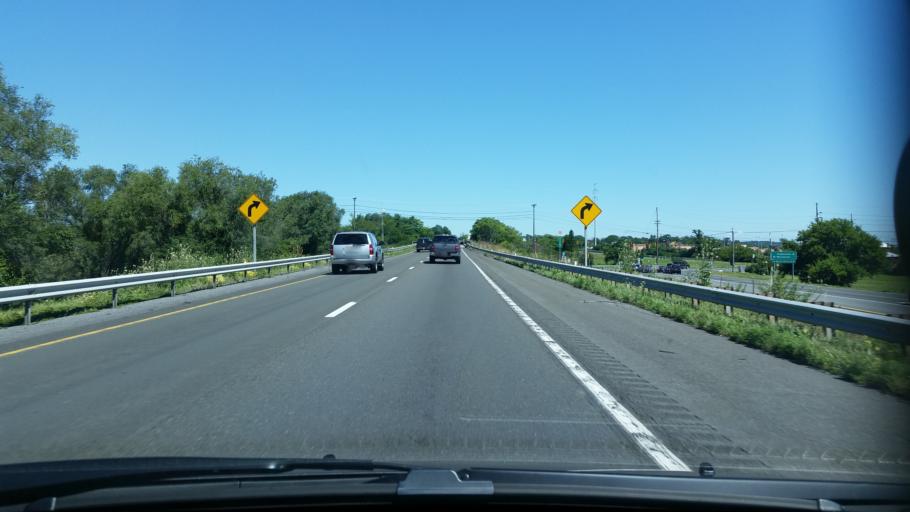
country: US
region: Virginia
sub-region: City of Winchester
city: Winchester
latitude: 39.2159
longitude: -78.1372
